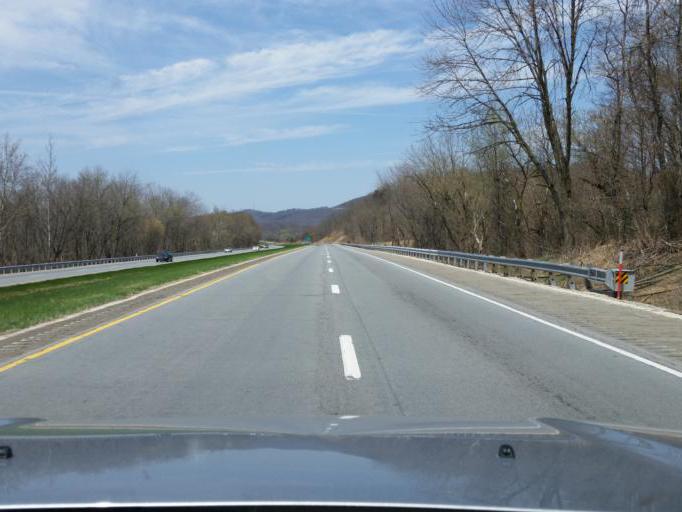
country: US
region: Pennsylvania
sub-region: Perry County
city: Newport
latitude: 40.5234
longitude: -77.1321
